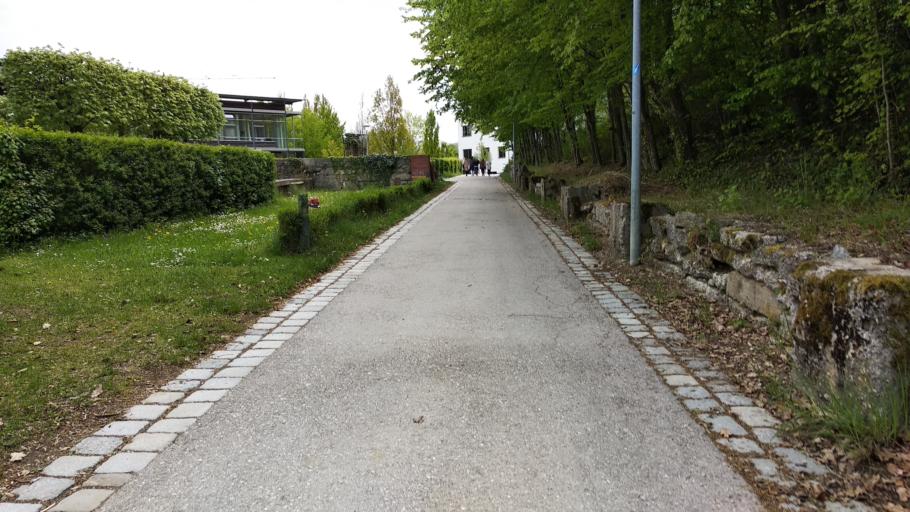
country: DE
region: Bavaria
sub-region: Upper Bavaria
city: Freising
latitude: 48.4001
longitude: 11.7195
